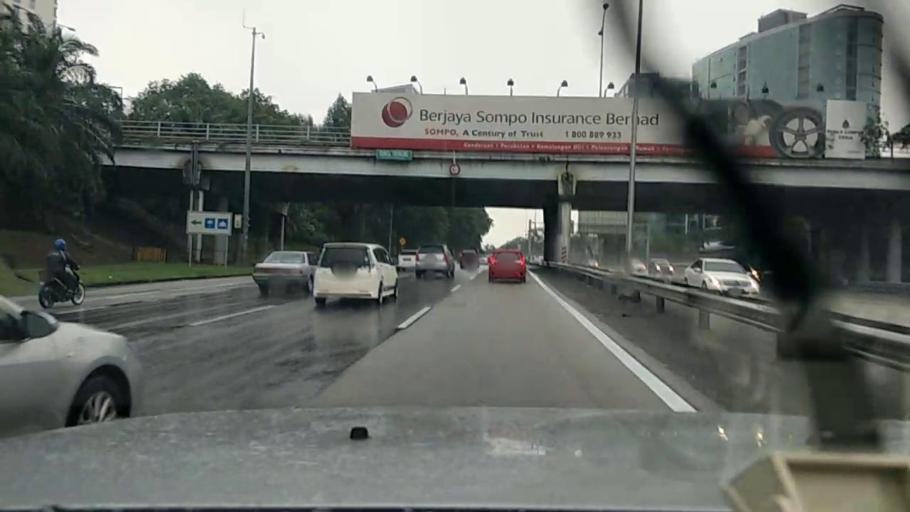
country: MY
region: Kuala Lumpur
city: Kuala Lumpur
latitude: 3.1048
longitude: 101.6940
